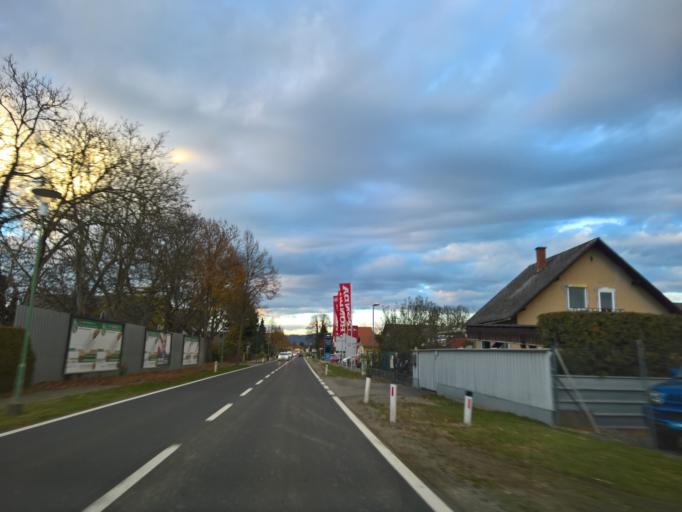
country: AT
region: Styria
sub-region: Politischer Bezirk Leibnitz
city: Kaindorf an der Sulm
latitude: 46.8088
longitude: 15.5512
